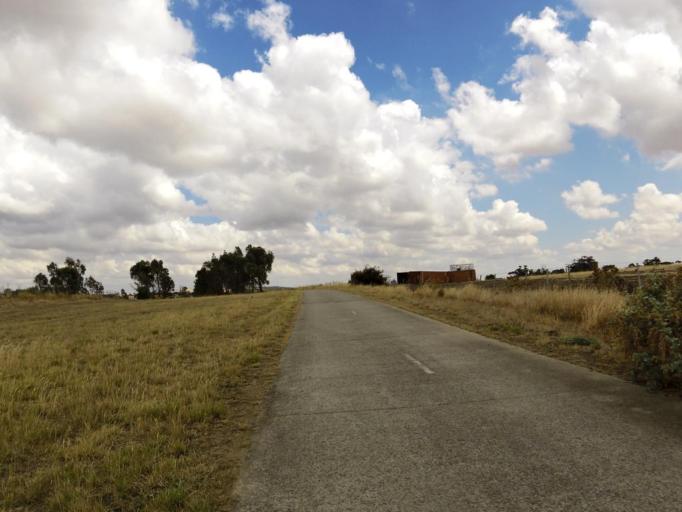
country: AU
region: Victoria
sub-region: Hume
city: Craigieburn
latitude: -37.6076
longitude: 144.9825
